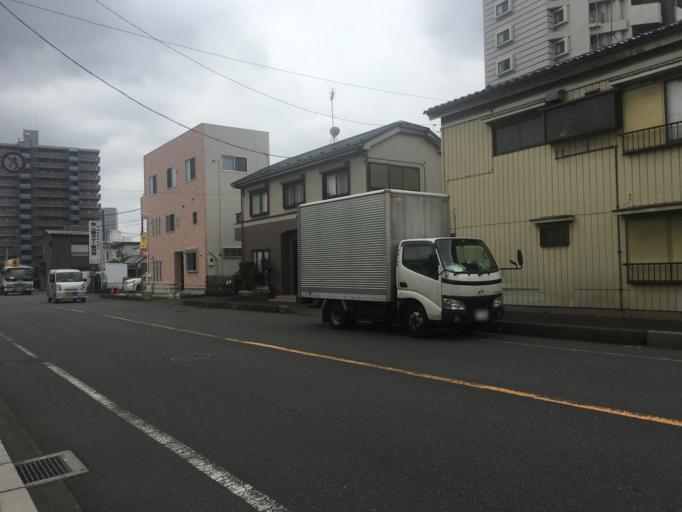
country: JP
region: Saitama
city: Kawaguchi
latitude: 35.8101
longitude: 139.7278
